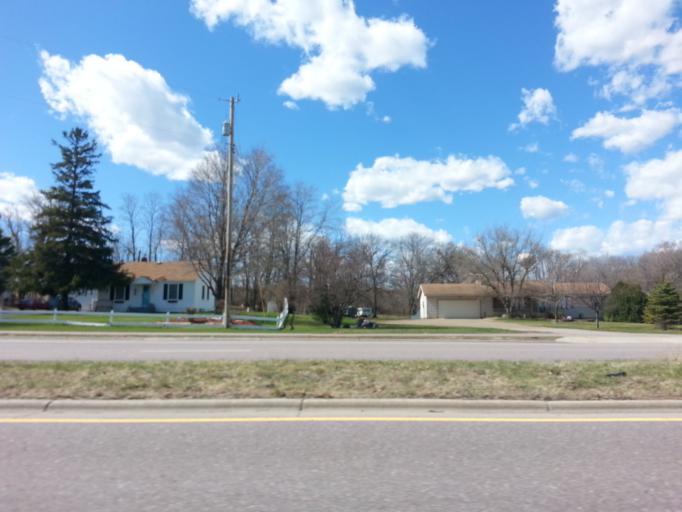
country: US
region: Minnesota
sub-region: Scott County
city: Prior Lake
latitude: 44.7194
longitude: -93.3781
